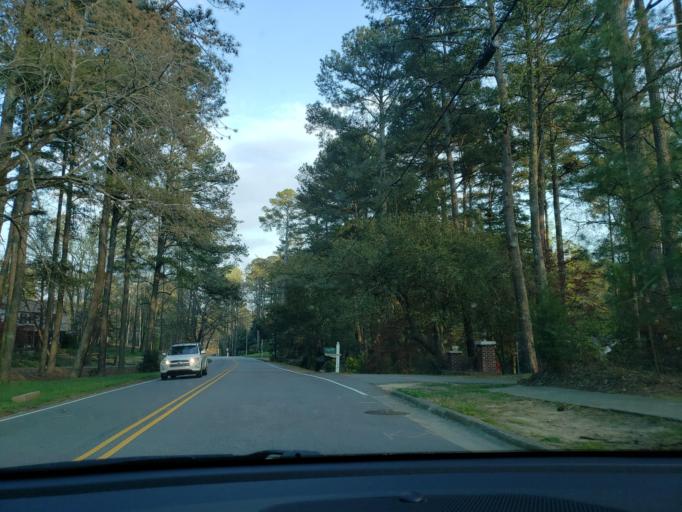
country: US
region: North Carolina
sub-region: Wake County
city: Apex
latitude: 35.7341
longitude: -78.8601
